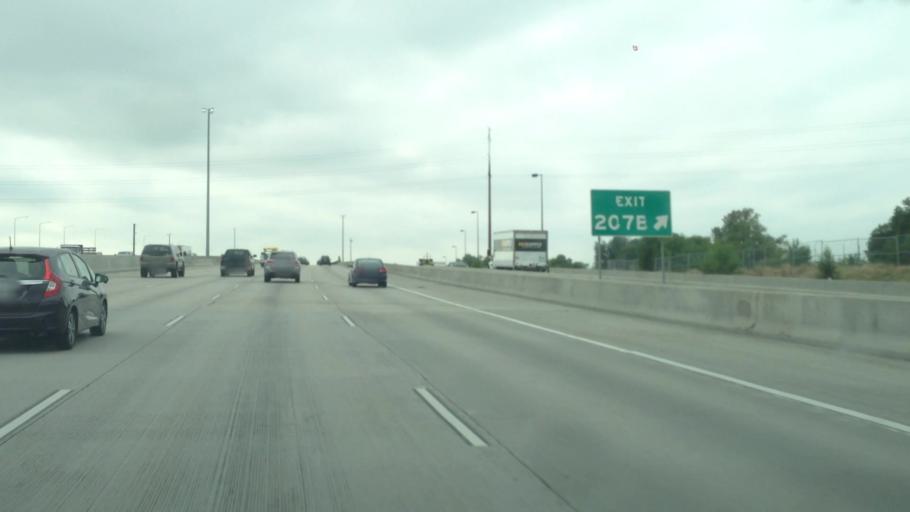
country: US
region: Colorado
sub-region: Denver County
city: Denver
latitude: 39.7098
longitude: -104.9984
